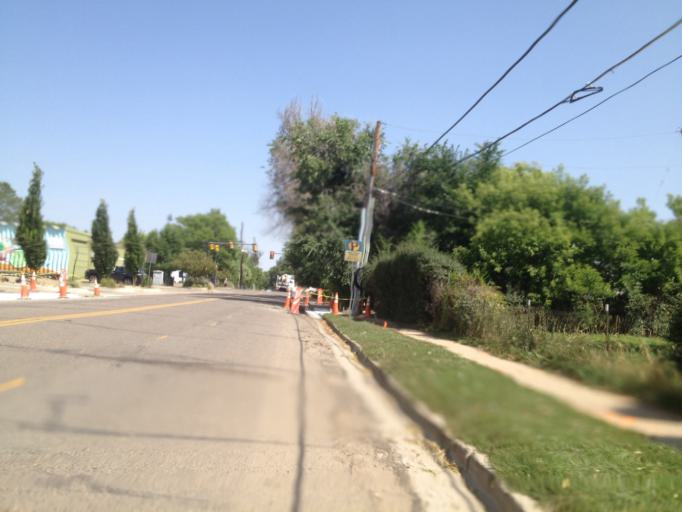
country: US
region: Colorado
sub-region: Boulder County
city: Lafayette
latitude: 39.9942
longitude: -105.0915
